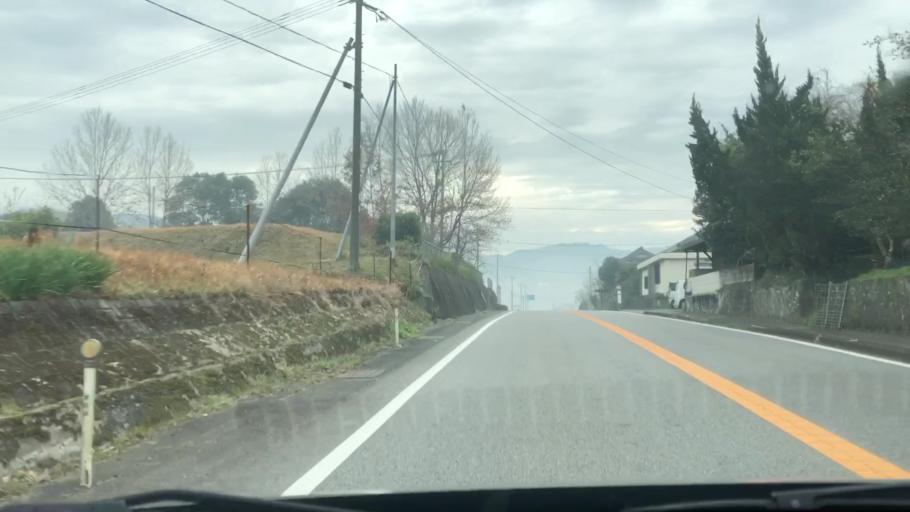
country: JP
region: Oita
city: Usuki
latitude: 33.0210
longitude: 131.6970
